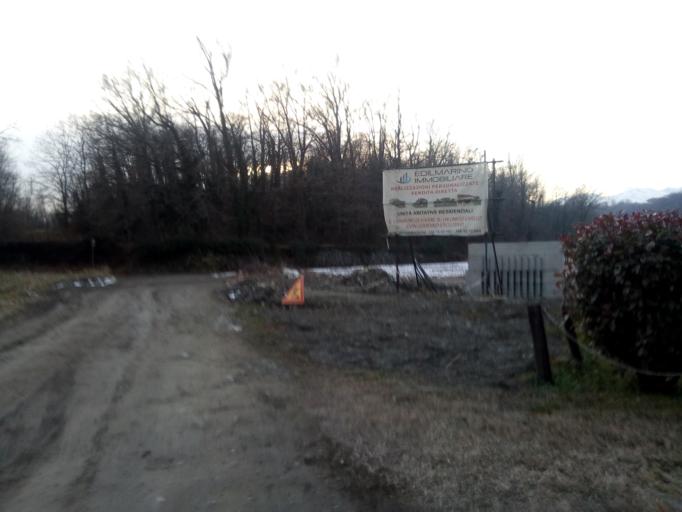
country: IT
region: Piedmont
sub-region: Provincia di Torino
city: Cascinette d'Ivrea
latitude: 45.4810
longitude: 7.9041
